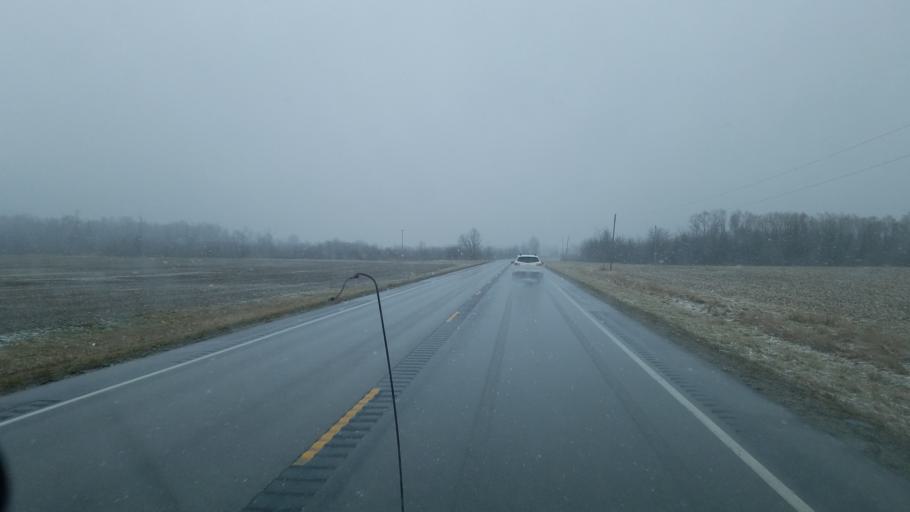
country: US
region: Indiana
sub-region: Grant County
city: Sweetser
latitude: 40.6544
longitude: -85.7120
